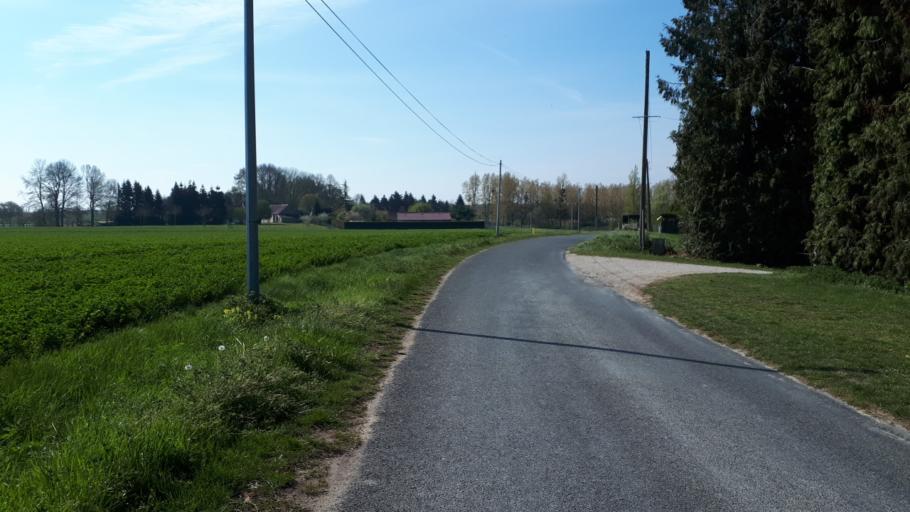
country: FR
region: Centre
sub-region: Departement du Loir-et-Cher
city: Contres
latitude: 47.3855
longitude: 1.3782
